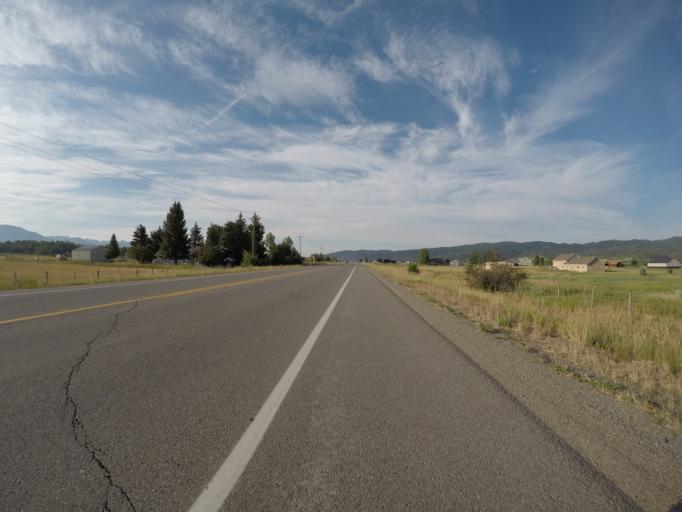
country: US
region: Wyoming
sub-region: Lincoln County
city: Afton
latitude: 42.9418
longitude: -111.0074
